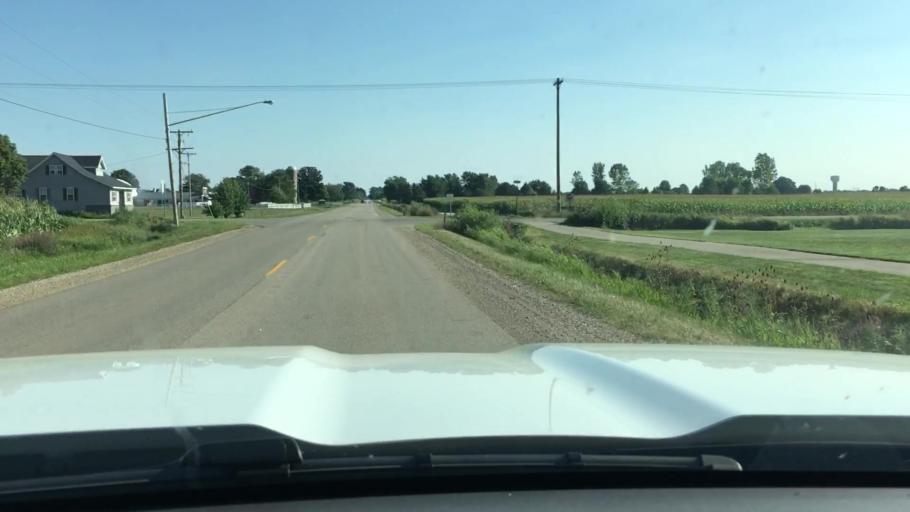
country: US
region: Michigan
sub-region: Ottawa County
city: Zeeland
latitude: 42.7979
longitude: -85.9402
